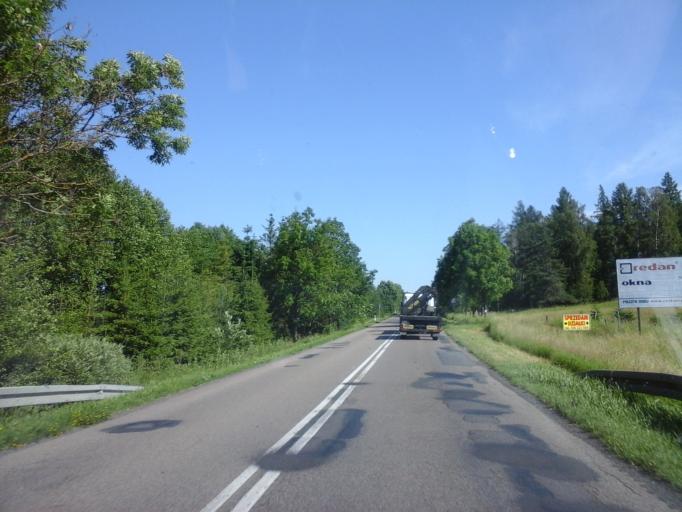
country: PL
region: West Pomeranian Voivodeship
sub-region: Powiat swidwinski
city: Polczyn-Zdroj
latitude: 53.7831
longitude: 16.0734
